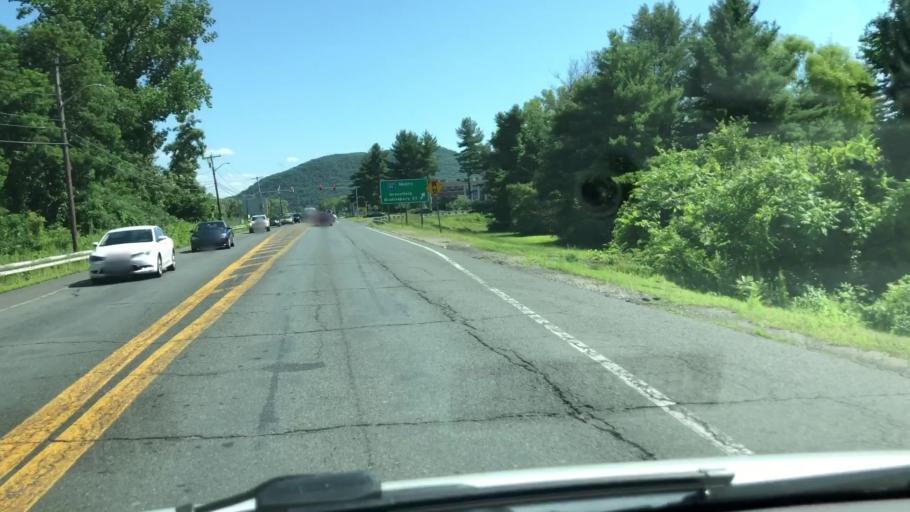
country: US
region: Massachusetts
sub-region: Hampshire County
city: Northampton
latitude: 42.3063
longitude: -72.6229
